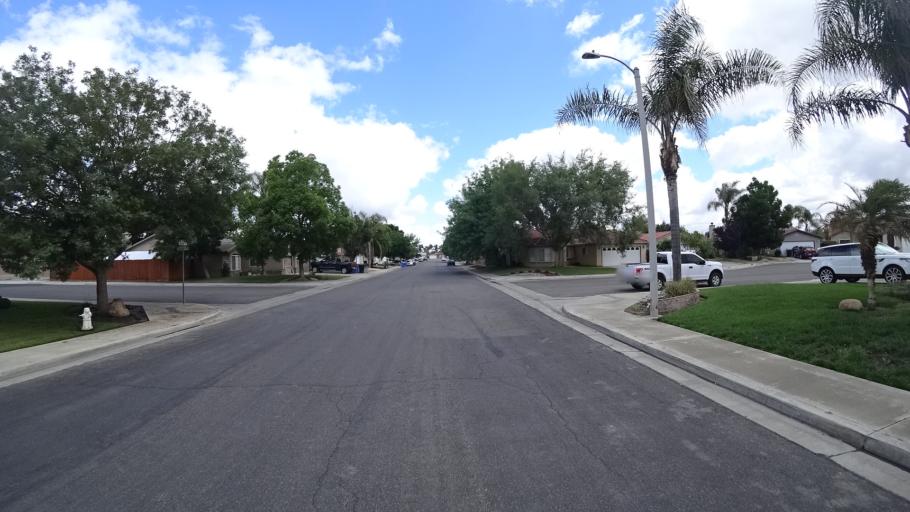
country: US
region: California
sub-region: Kings County
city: Lucerne
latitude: 36.3543
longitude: -119.6591
